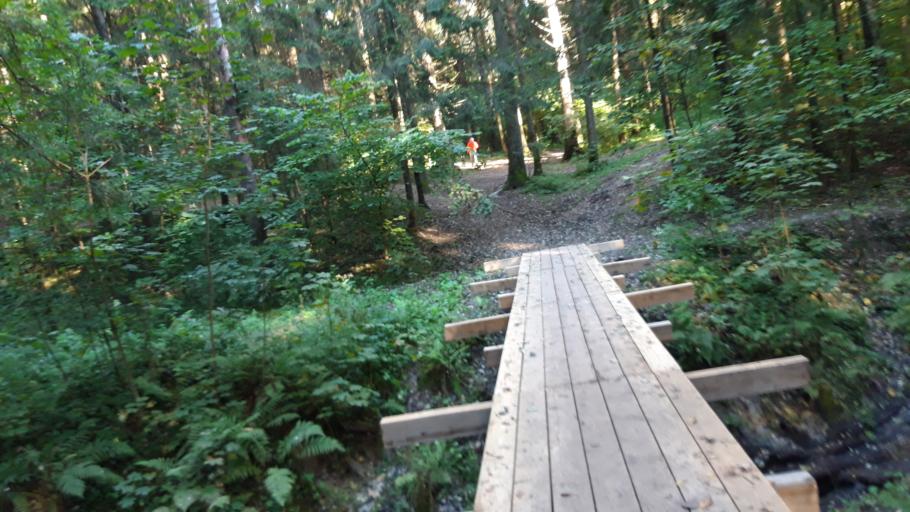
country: RU
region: Moscow
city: Zelenograd
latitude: 55.9854
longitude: 37.1965
